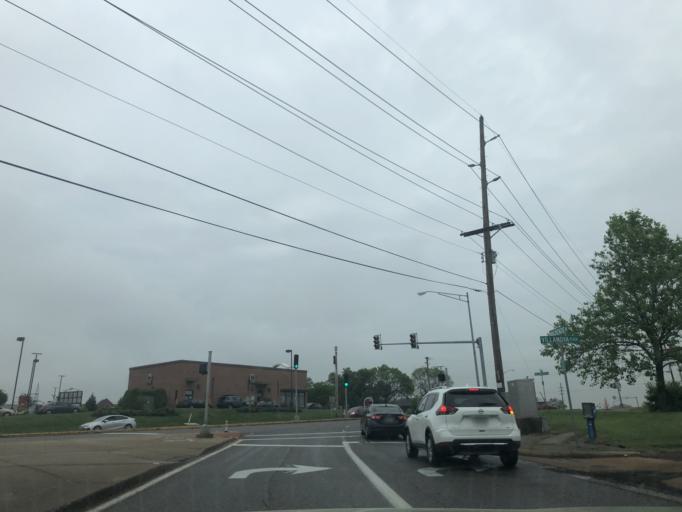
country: US
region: Missouri
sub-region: Saint Louis County
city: Shrewsbury
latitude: 38.5830
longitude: -90.3179
